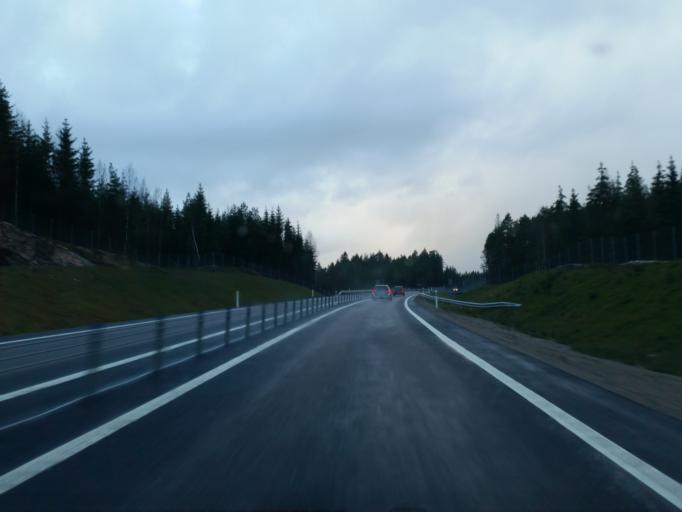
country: SE
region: Vaestra Goetaland
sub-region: Boras Kommun
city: Boras
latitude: 57.6831
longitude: 12.9330
